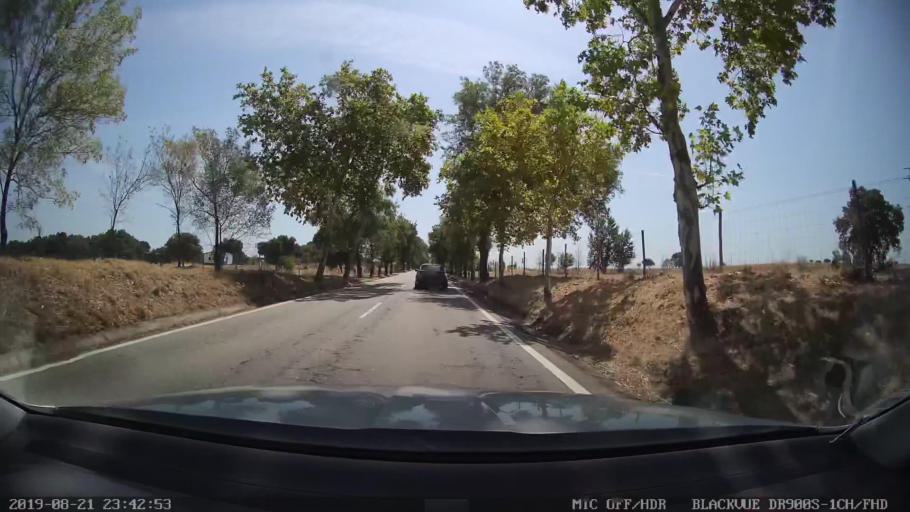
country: PT
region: Castelo Branco
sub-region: Idanha-A-Nova
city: Idanha-a-Nova
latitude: 39.8529
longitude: -7.3046
